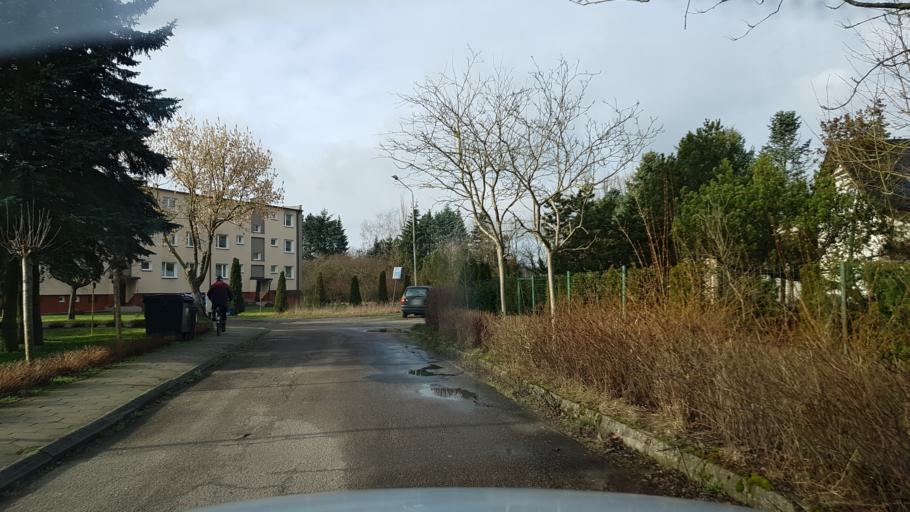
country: PL
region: West Pomeranian Voivodeship
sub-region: Powiat swidwinski
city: Rabino
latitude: 53.7766
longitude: 15.9565
